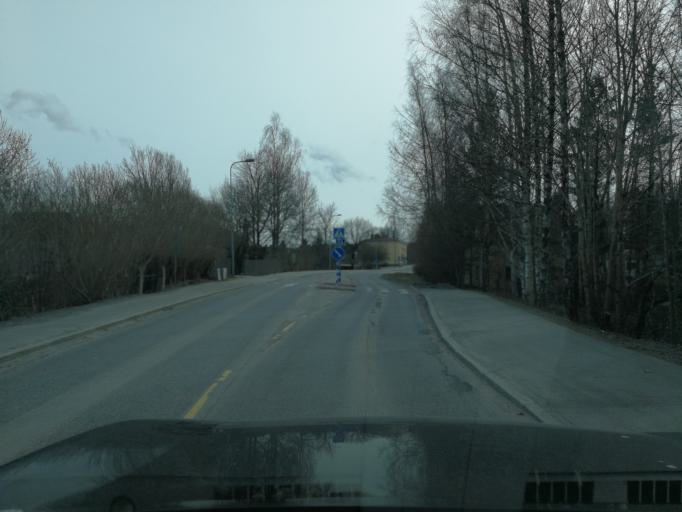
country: FI
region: Uusimaa
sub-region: Helsinki
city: Lohja
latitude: 60.1947
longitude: 24.0020
